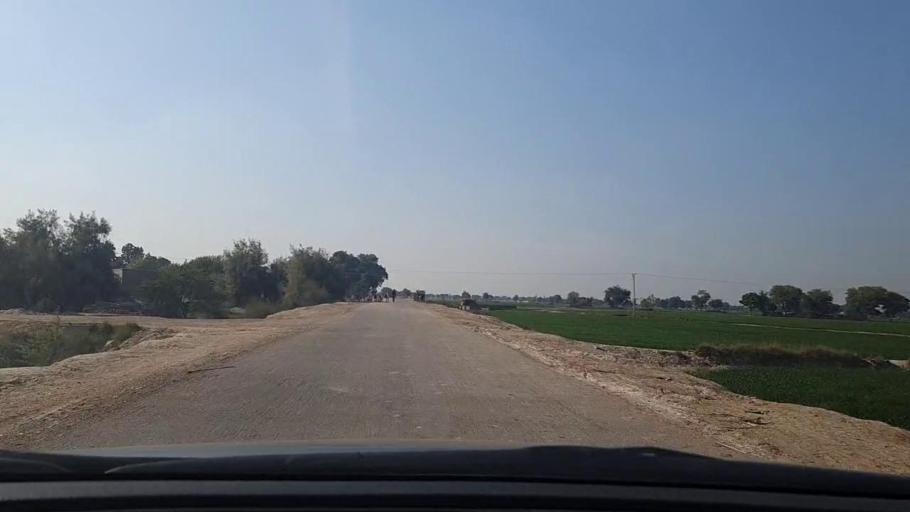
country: PK
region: Sindh
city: Daulatpur
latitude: 26.3175
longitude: 68.0578
